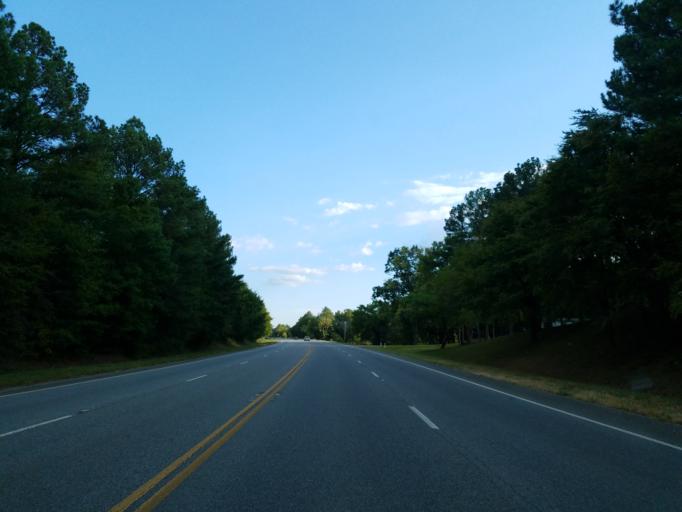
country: US
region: Georgia
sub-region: Murray County
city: Chatsworth
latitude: 34.7041
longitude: -84.7422
